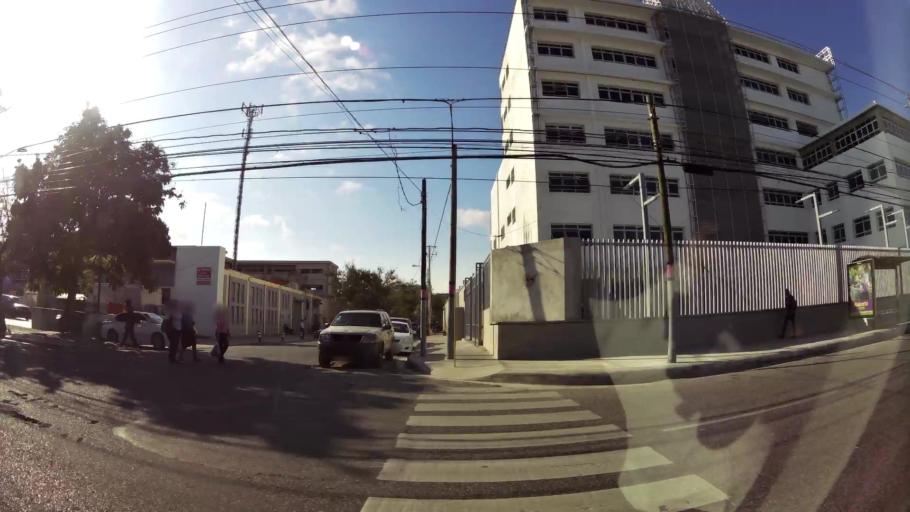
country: DO
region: Nacional
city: Bella Vista
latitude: 18.4489
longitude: -69.9310
